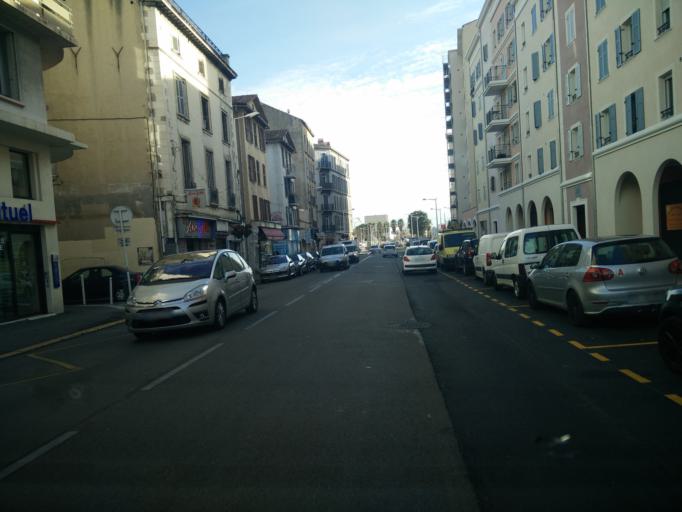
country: FR
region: Provence-Alpes-Cote d'Azur
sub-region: Departement du Var
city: Toulon
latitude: 43.1284
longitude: 5.9163
